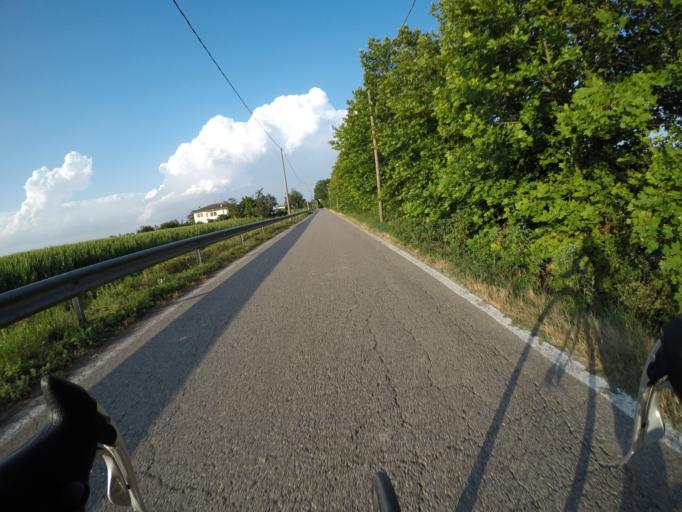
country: IT
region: Veneto
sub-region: Provincia di Rovigo
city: Villanova del Ghebbo Canton
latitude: 45.0521
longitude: 11.6174
